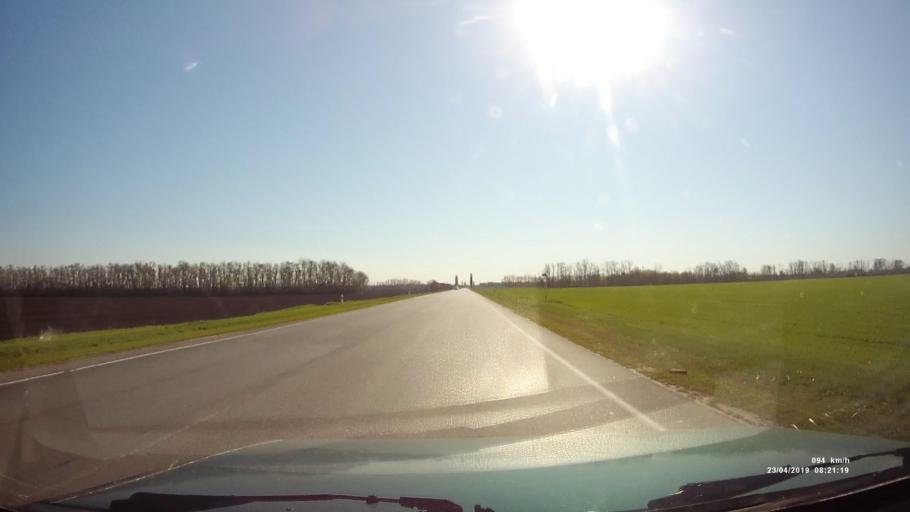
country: RU
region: Rostov
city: Tselina
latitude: 46.5357
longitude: 40.8889
